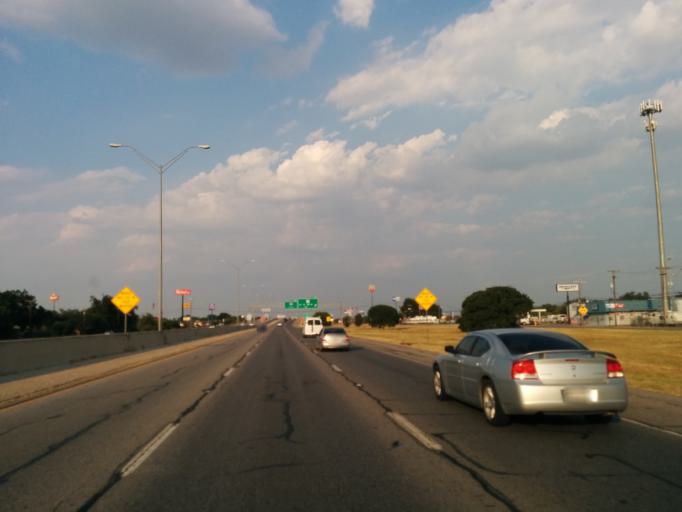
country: US
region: Texas
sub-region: Bexar County
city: Kirby
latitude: 29.4301
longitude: -98.4112
